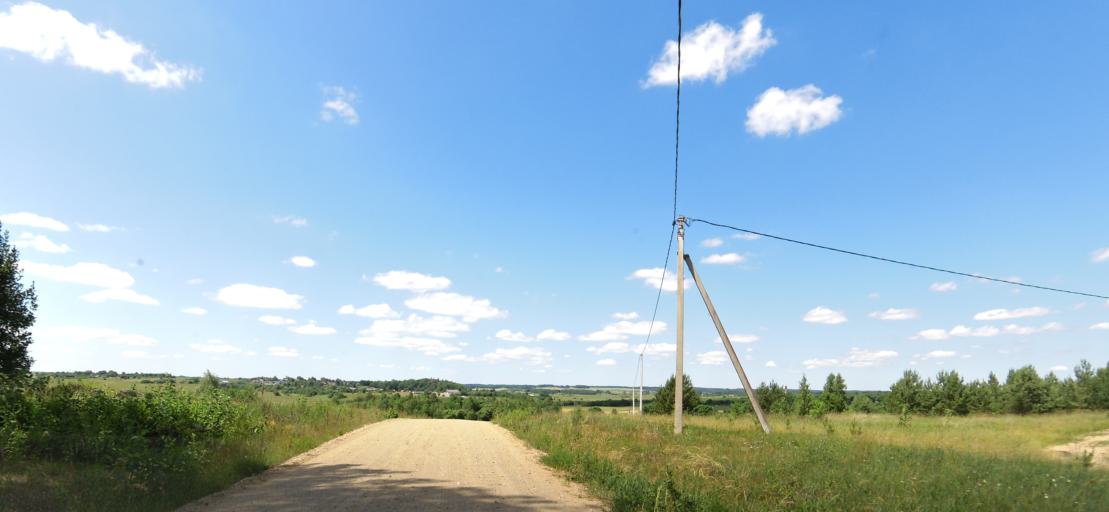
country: LT
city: Nemencine
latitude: 54.8929
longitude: 25.5032
